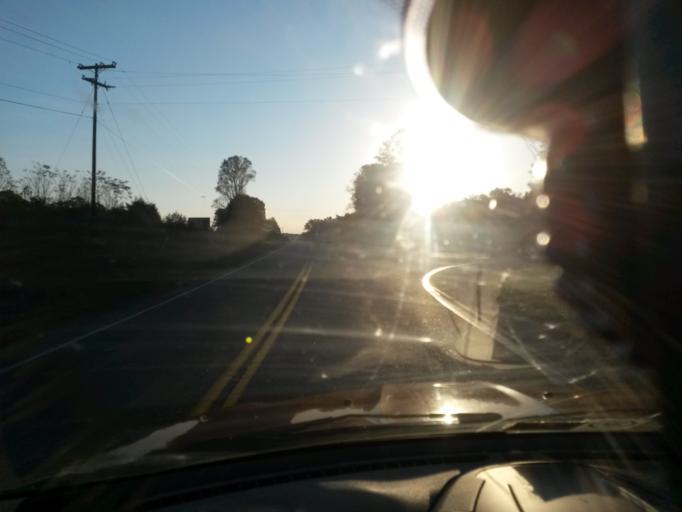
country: US
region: Virginia
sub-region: Franklin County
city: North Shore
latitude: 37.1221
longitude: -79.7367
